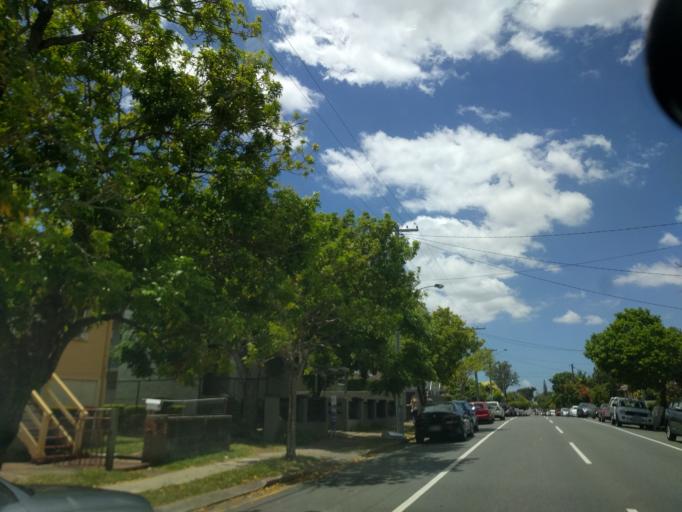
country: AU
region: Queensland
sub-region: Brisbane
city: Fortitude Valley
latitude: -27.4610
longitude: 153.0411
